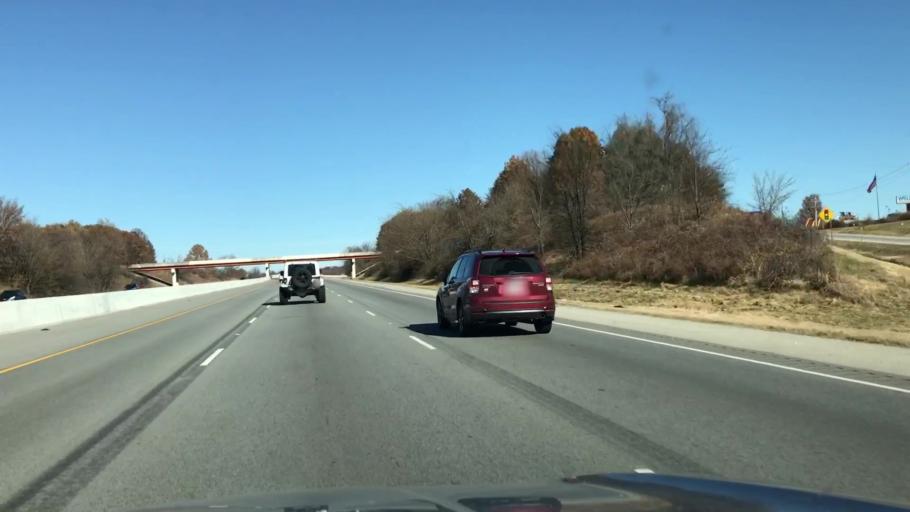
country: US
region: Arkansas
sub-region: Benton County
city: Bethel Heights
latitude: 36.2238
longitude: -94.1795
